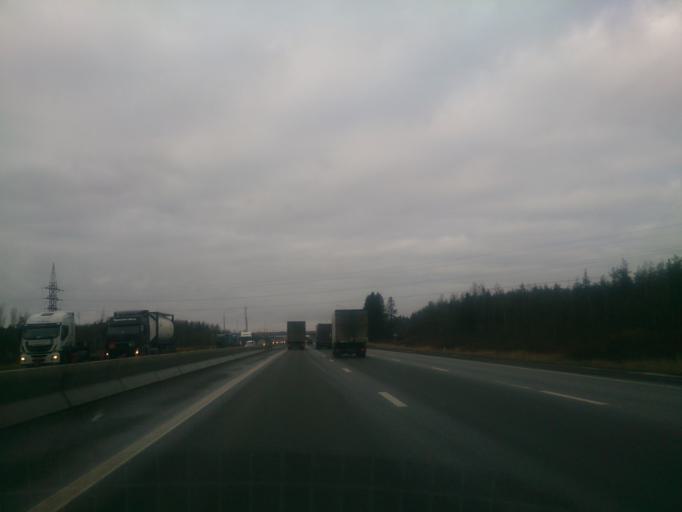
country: RU
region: Leningrad
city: Ul'yanovka
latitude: 59.6027
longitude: 30.7644
